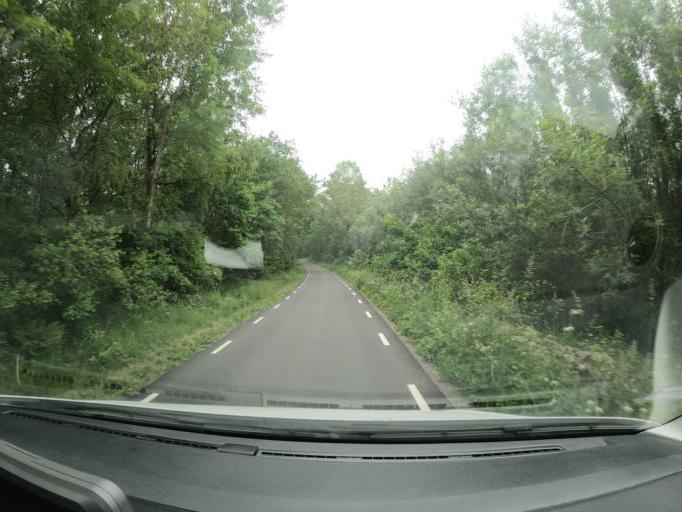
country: SE
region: Skane
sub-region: Perstorps Kommun
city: Perstorp
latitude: 56.0237
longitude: 13.3470
